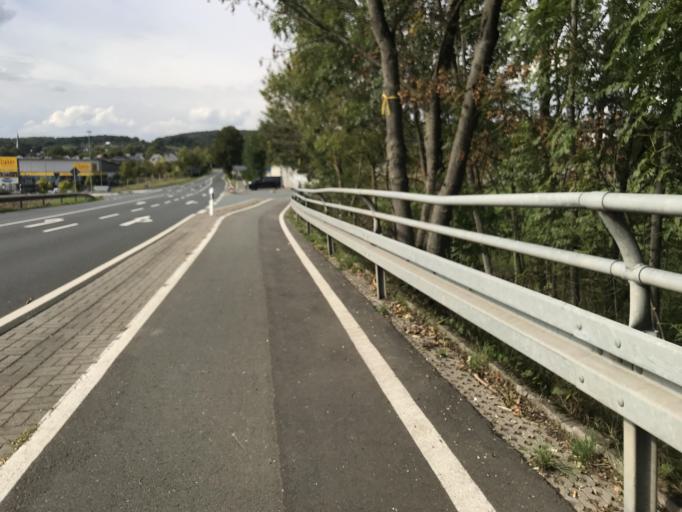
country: DE
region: Hesse
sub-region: Regierungsbezirk Giessen
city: Asslar
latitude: 50.5981
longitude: 8.4273
